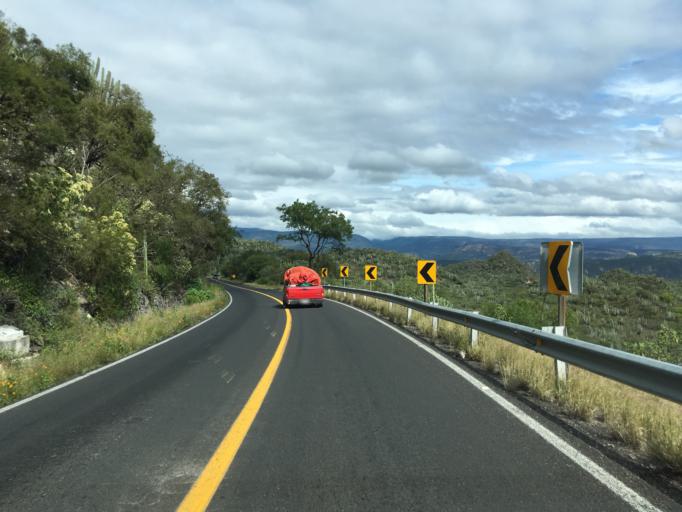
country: MX
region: Hidalgo
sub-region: San Agustin Metzquititlan
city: Mezquititlan
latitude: 20.4367
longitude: -98.6841
